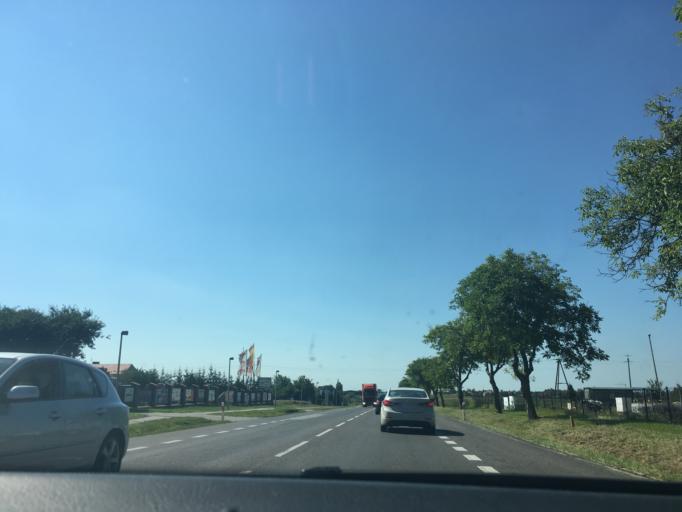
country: PL
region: Lublin Voivodeship
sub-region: Powiat lubelski
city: Niemce
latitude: 51.3472
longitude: 22.6195
